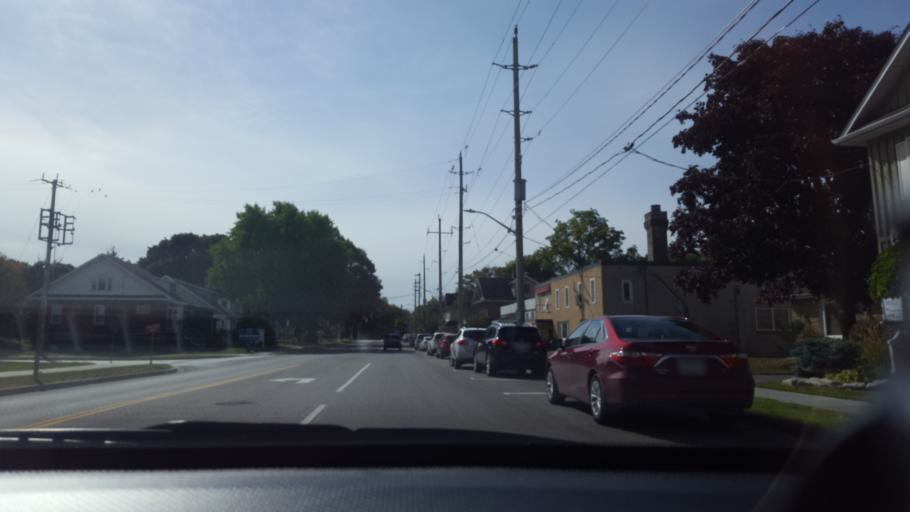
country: CA
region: Ontario
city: Newmarket
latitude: 44.0595
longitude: -79.4539
